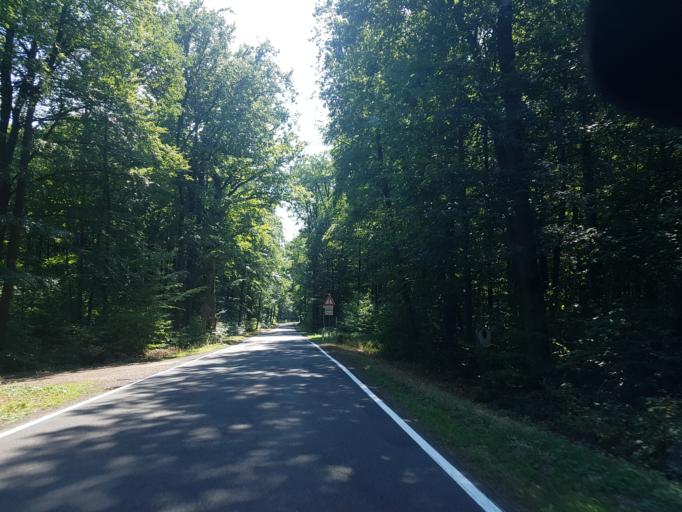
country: DE
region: Brandenburg
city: Wiesenburg
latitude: 52.0453
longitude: 12.3777
